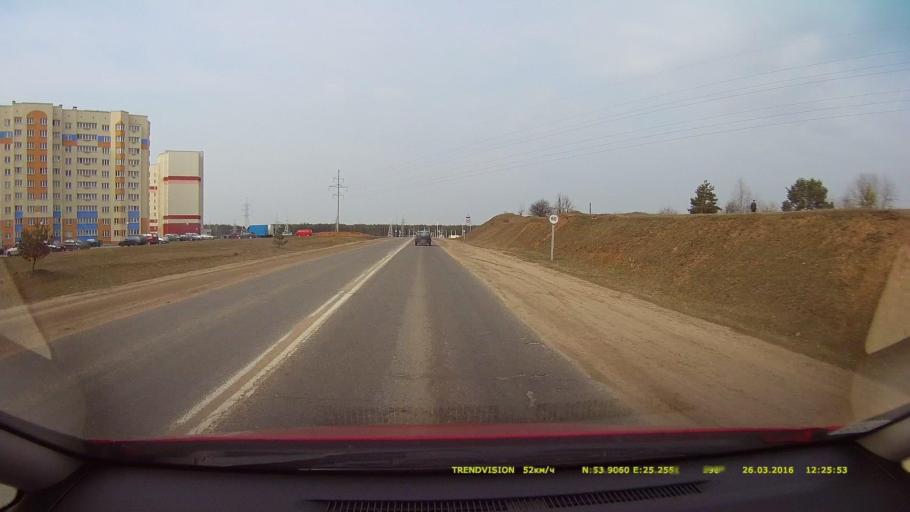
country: BY
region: Grodnenskaya
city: Lida
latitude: 53.9060
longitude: 25.2551
